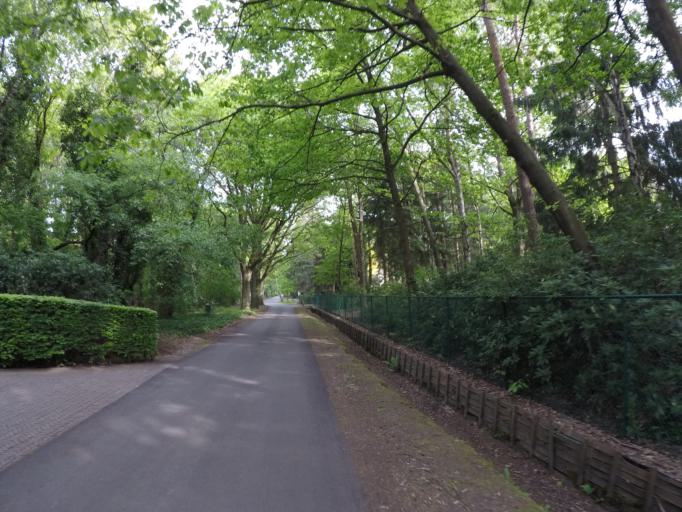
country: BE
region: Flanders
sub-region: Provincie Antwerpen
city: Kapellen
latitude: 51.3531
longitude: 4.4408
